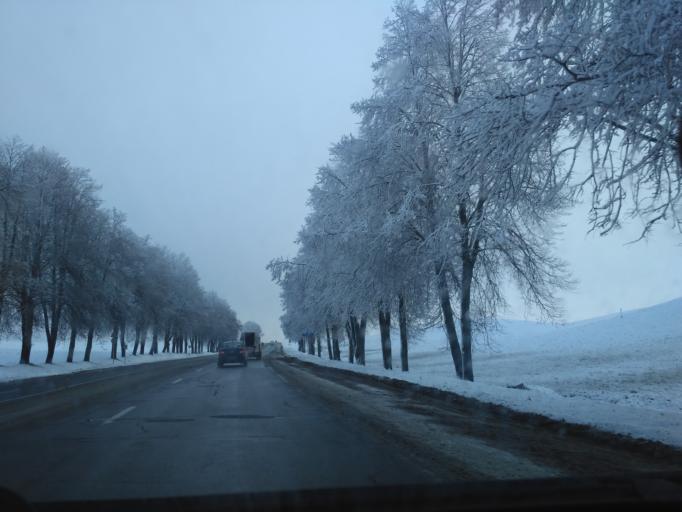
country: BY
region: Minsk
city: Horad Smalyavichy
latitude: 54.0474
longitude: 28.0702
